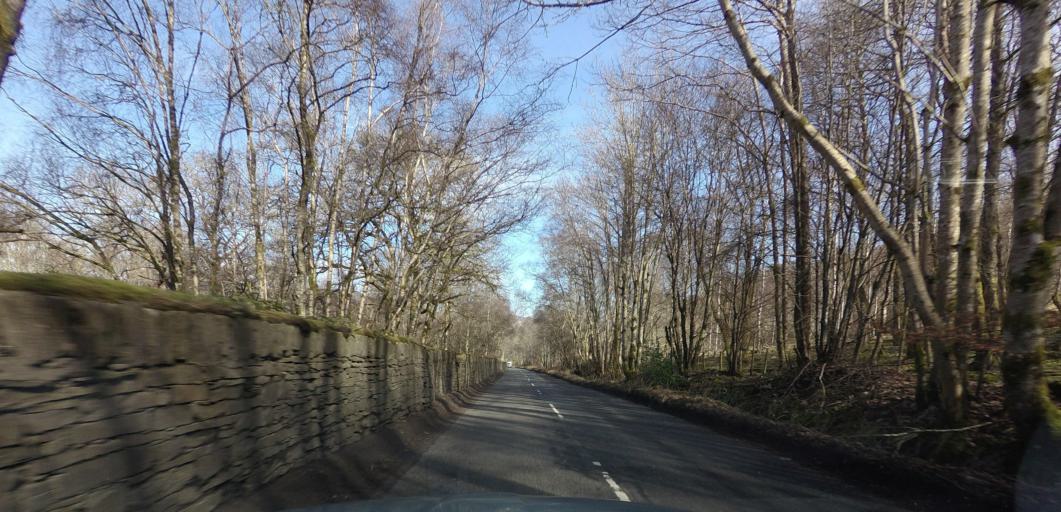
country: GB
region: Scotland
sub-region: Perth and Kinross
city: Aberfeldy
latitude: 56.5946
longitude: -3.9683
